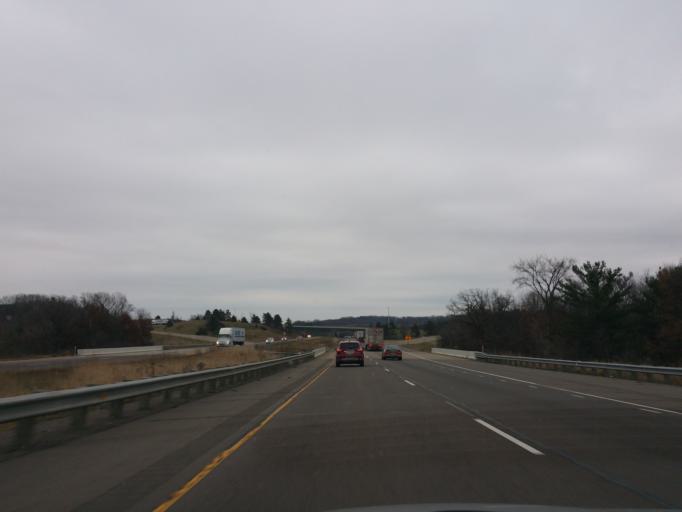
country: US
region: Wisconsin
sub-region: Trempealeau County
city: Osseo
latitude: 44.4634
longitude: -91.0964
